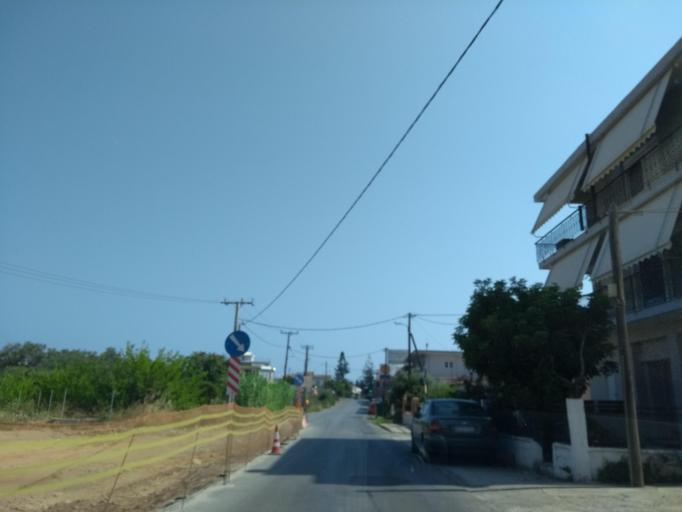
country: GR
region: Crete
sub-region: Nomos Chanias
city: Chania
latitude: 35.5007
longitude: 24.0189
